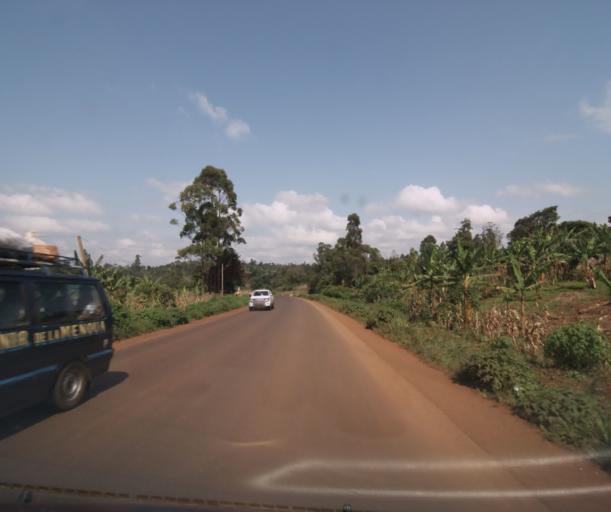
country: CM
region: West
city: Bansoa
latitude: 5.5007
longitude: 10.2374
